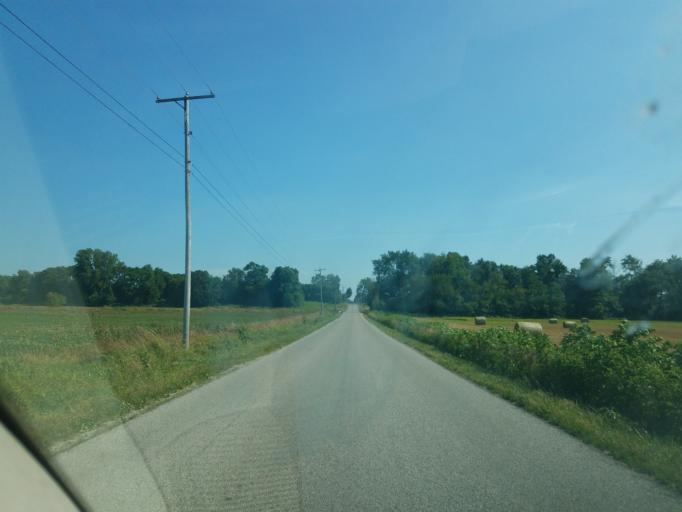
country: US
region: Ohio
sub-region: Morrow County
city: Mount Gilead
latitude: 40.6323
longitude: -82.8602
